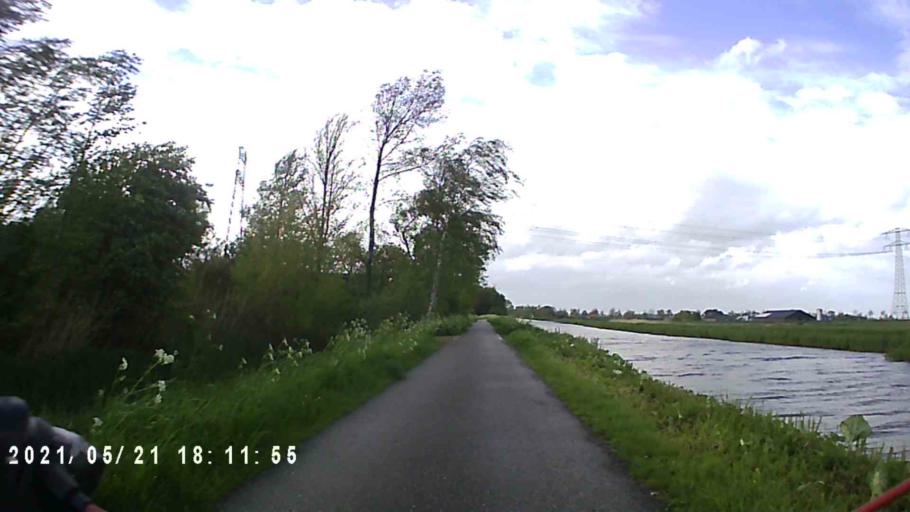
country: NL
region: Groningen
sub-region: Gemeente Zuidhorn
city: Zuidhorn
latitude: 53.2086
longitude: 6.4115
